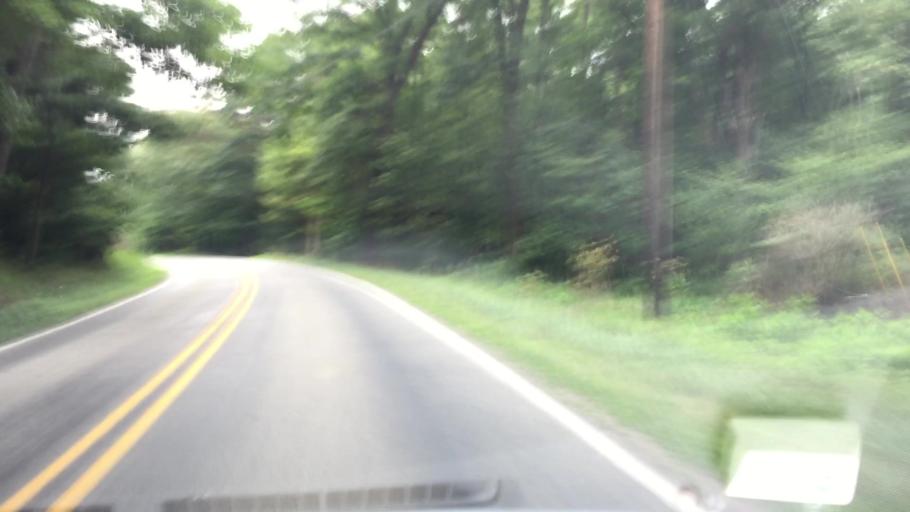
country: US
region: Pennsylvania
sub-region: Allegheny County
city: Curtisville
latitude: 40.7007
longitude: -79.8462
